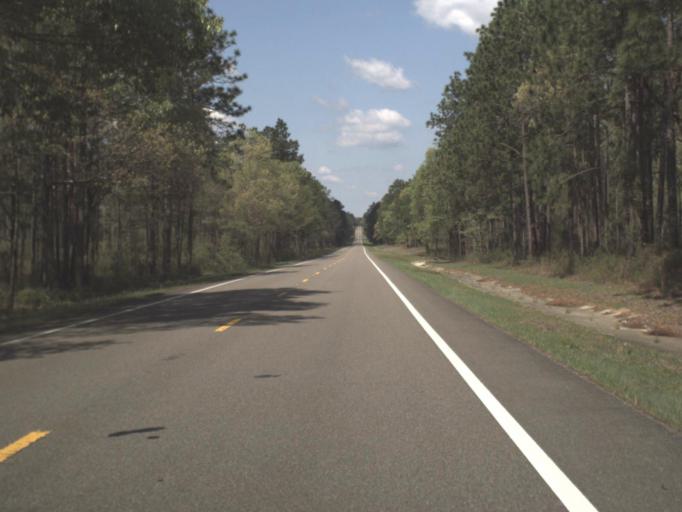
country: US
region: Florida
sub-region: Okaloosa County
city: Crestview
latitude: 30.8517
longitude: -86.8113
